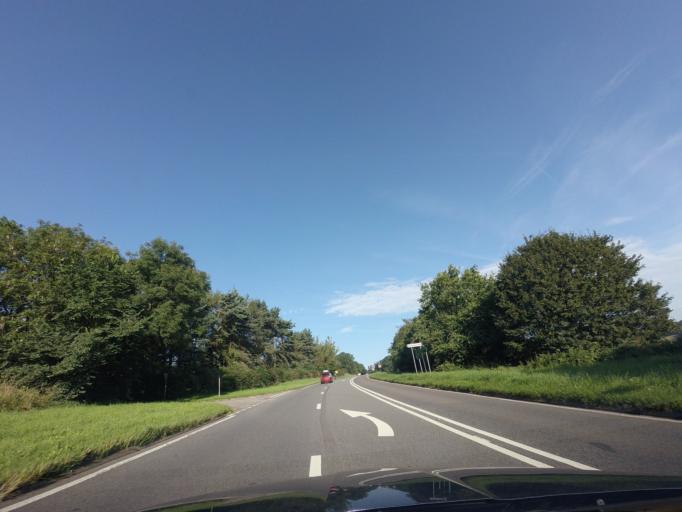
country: GB
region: England
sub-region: Derbyshire
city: Wingerworth
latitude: 53.2297
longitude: -1.5101
